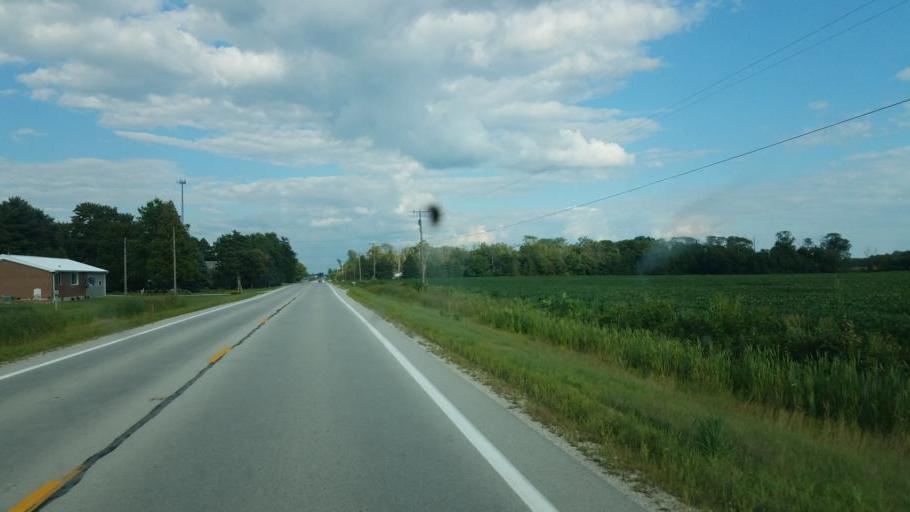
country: US
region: Ohio
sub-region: Sandusky County
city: Gibsonburg
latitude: 41.3413
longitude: -83.3753
